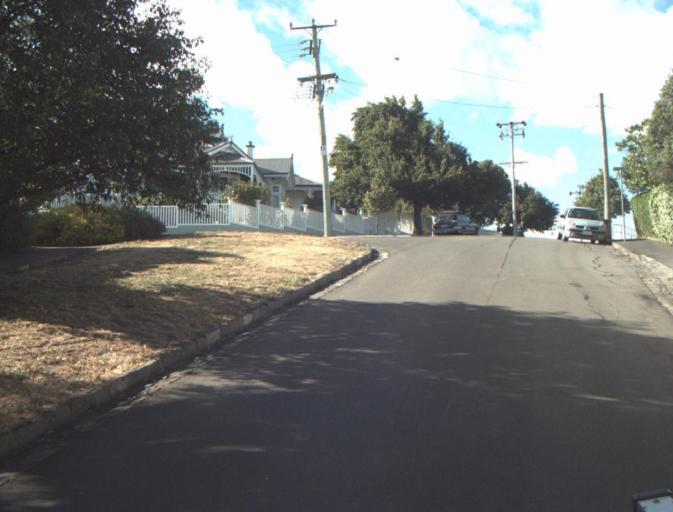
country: AU
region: Tasmania
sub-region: Launceston
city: East Launceston
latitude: -41.4396
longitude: 147.1544
